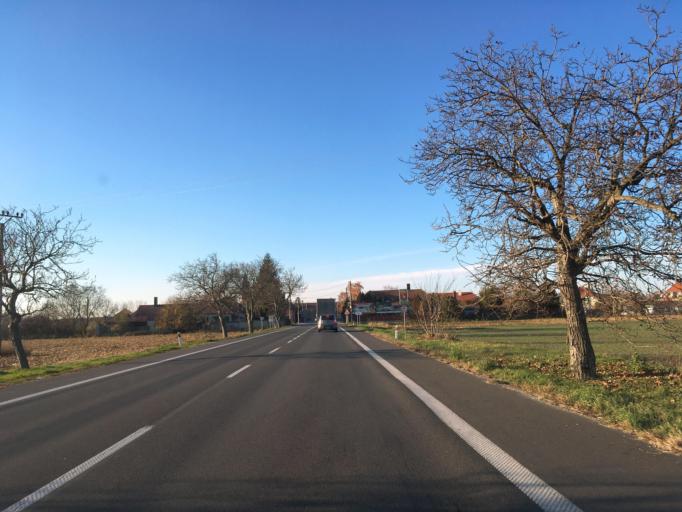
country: SK
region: Trnavsky
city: Dunajska Streda
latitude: 47.9645
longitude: 17.6895
